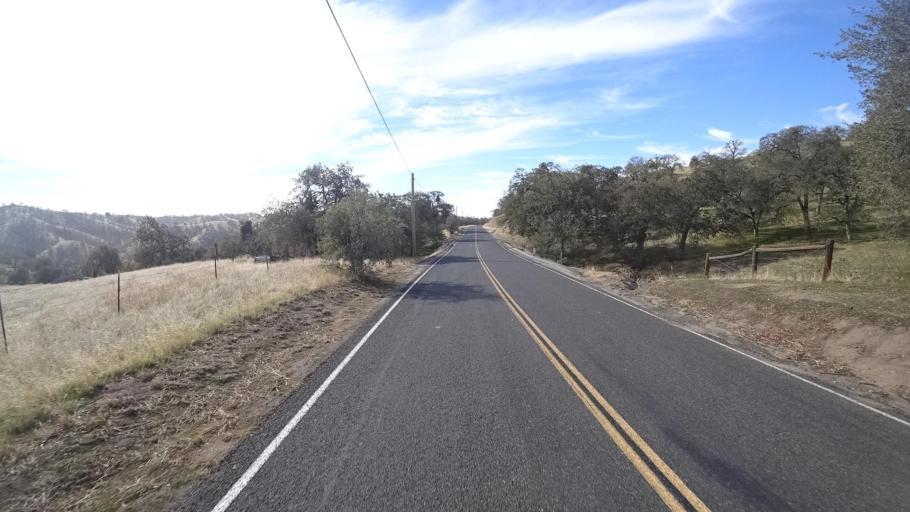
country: US
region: California
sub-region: Kern County
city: Alta Sierra
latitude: 35.6293
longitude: -118.8012
